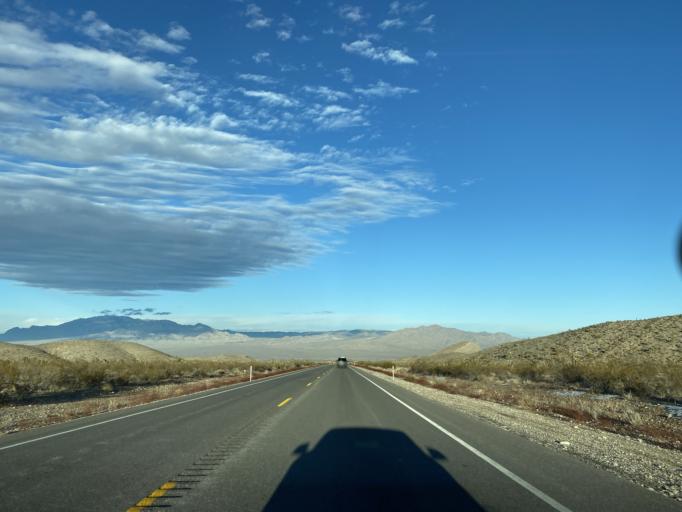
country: US
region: Nevada
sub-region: Clark County
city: Summerlin South
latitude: 36.2871
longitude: -115.4332
